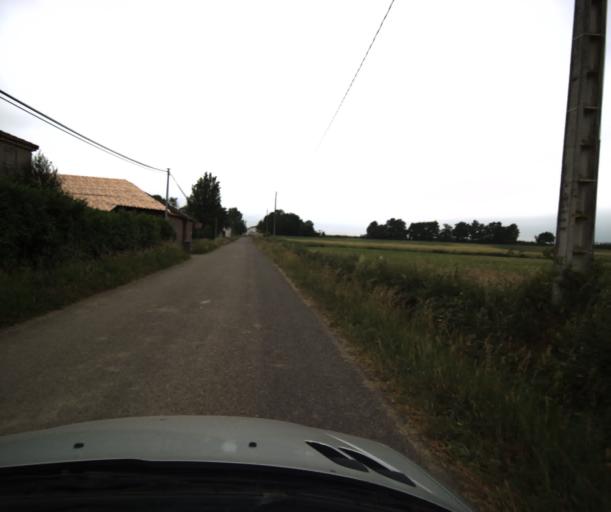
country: FR
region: Midi-Pyrenees
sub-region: Departement du Tarn-et-Garonne
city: Saint-Nicolas-de-la-Grave
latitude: 44.0562
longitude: 0.9991
